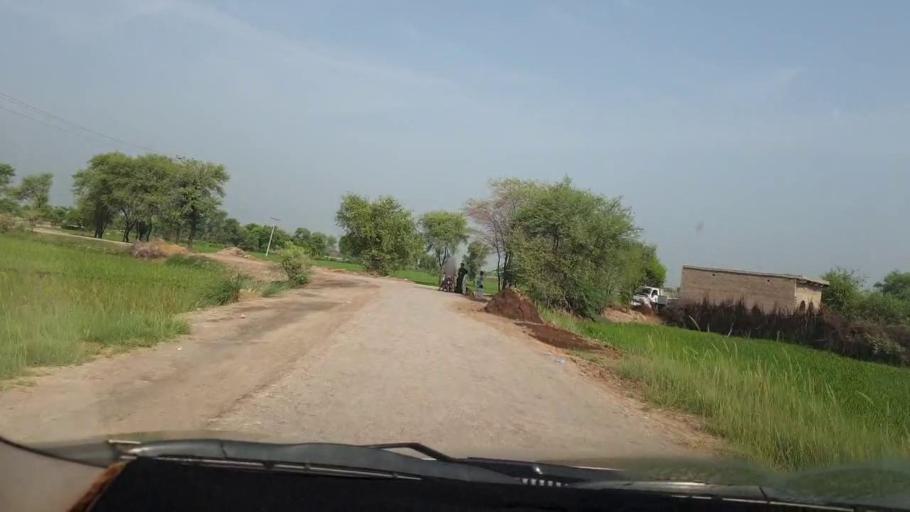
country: PK
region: Sindh
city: Goth Garelo
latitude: 27.4500
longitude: 68.0249
